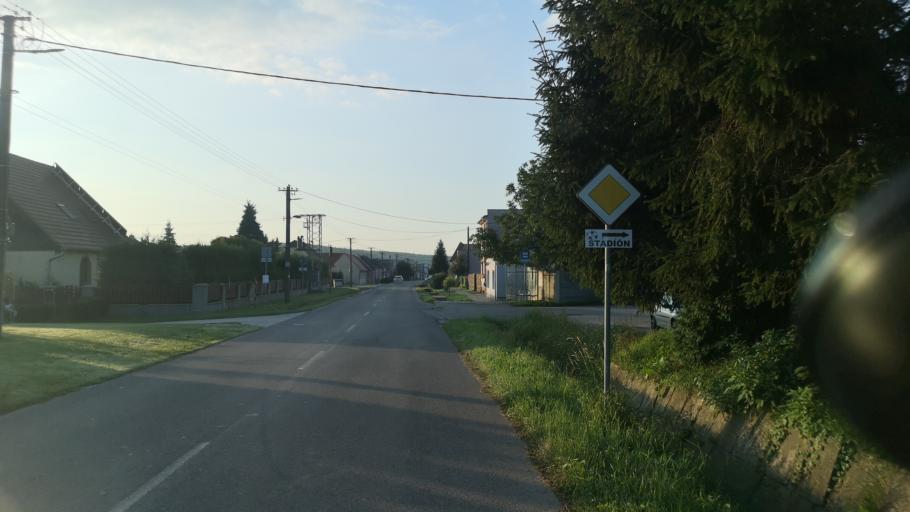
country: SK
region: Trnavsky
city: Smolenice
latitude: 48.5200
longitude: 17.5216
